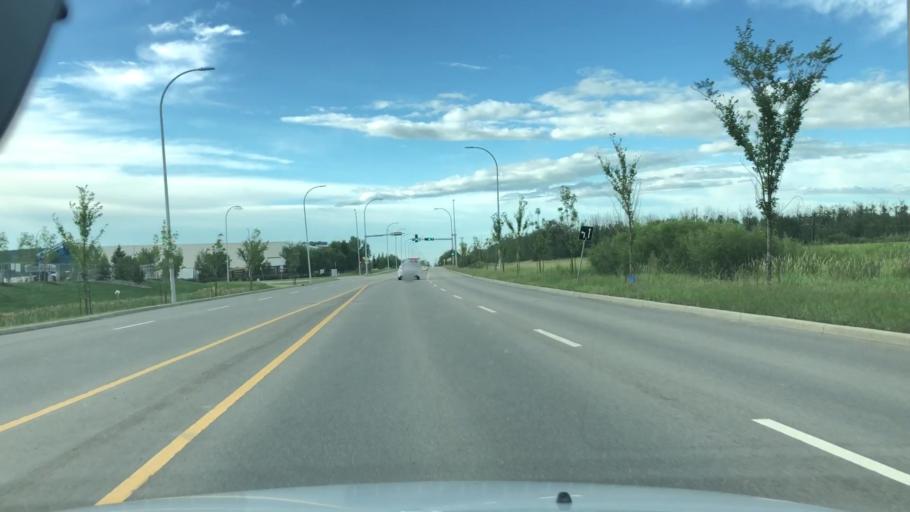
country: CA
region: Alberta
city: St. Albert
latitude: 53.6346
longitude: -113.5658
